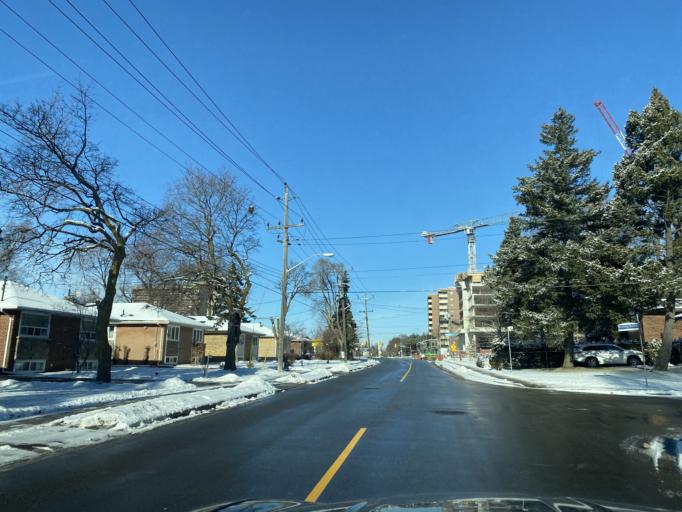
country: CA
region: Ontario
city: Scarborough
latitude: 43.7747
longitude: -79.3168
